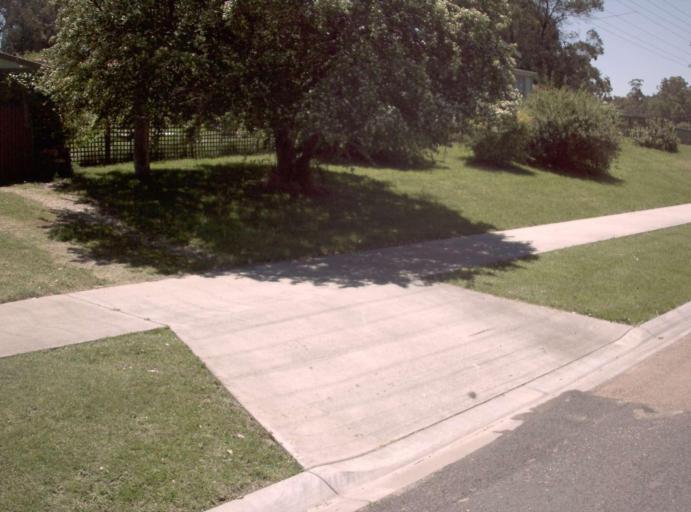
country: AU
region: Victoria
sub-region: East Gippsland
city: Lakes Entrance
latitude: -37.7332
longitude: 148.0903
